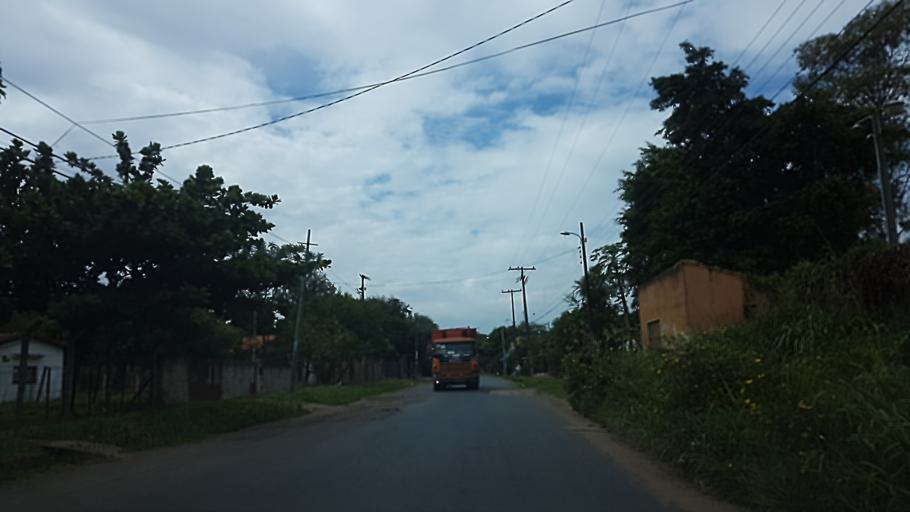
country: PY
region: Central
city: San Lorenzo
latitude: -25.2812
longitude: -57.4957
